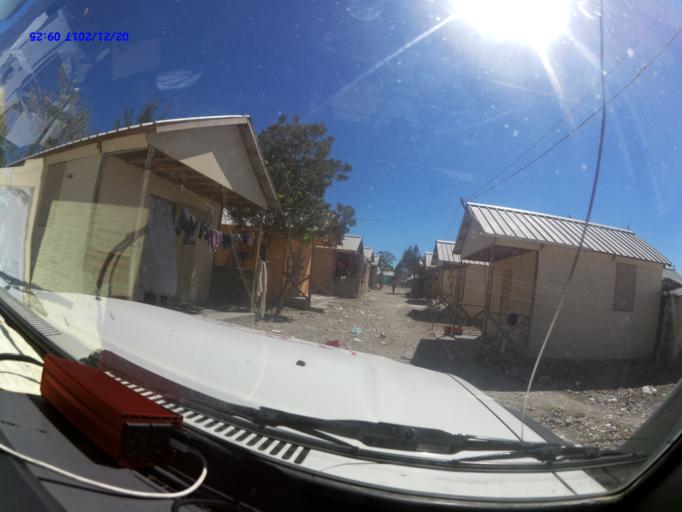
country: HT
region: Ouest
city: Croix des Bouquets
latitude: 18.6553
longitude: -72.2518
